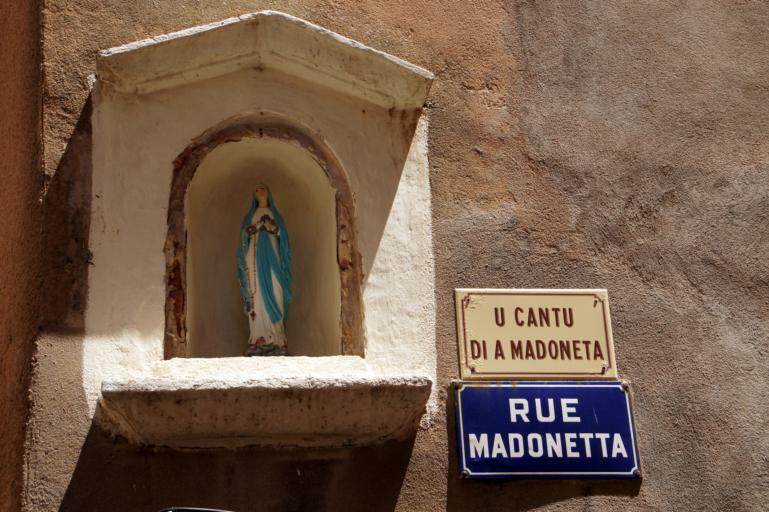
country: FR
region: Corsica
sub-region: Departement de la Corse-du-Sud
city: Bonifacio
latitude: 41.3868
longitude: 9.1593
